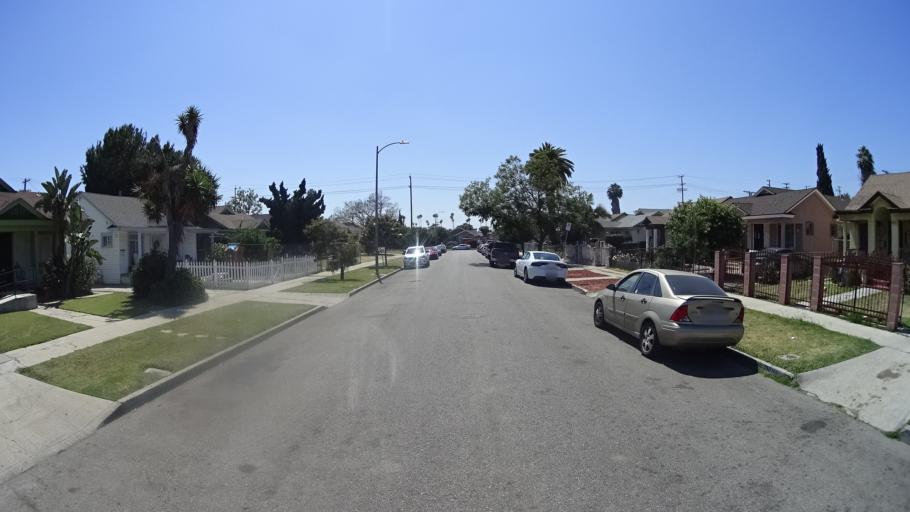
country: US
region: California
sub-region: Los Angeles County
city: View Park-Windsor Hills
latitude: 34.0174
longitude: -118.3151
